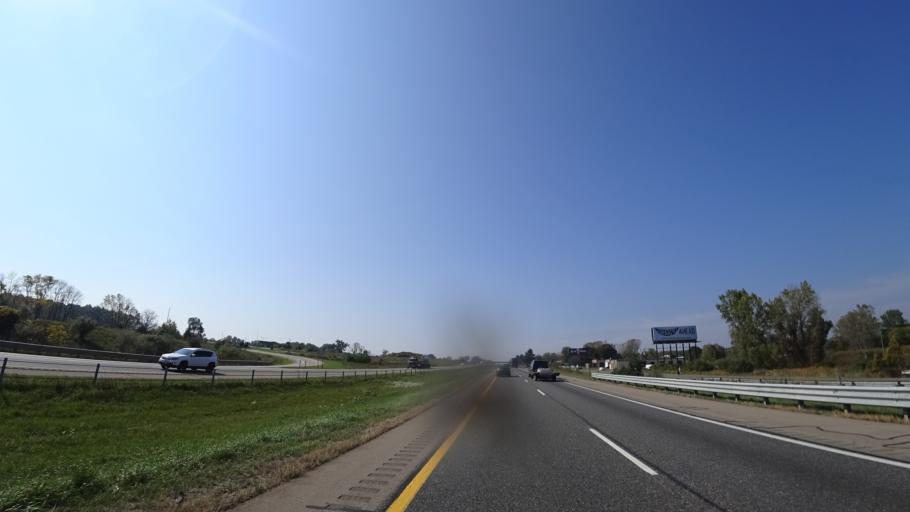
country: US
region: Michigan
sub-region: Washtenaw County
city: Chelsea
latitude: 42.2966
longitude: -83.9962
